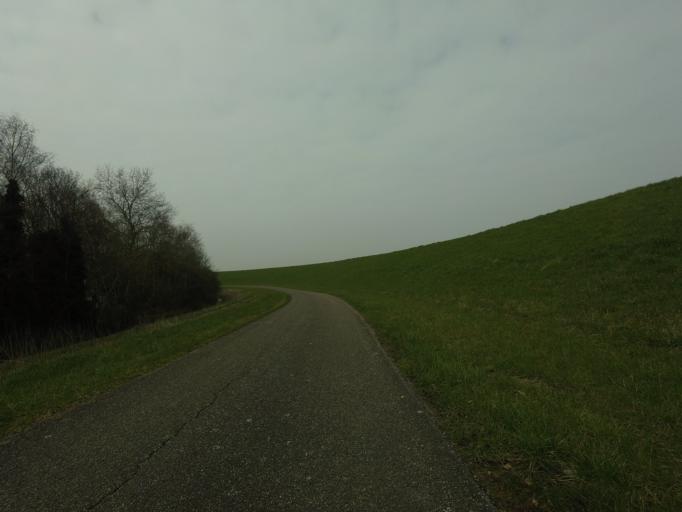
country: NL
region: North Brabant
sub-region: Gemeente Woensdrecht
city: Woensdrecht
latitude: 51.3508
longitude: 4.2258
